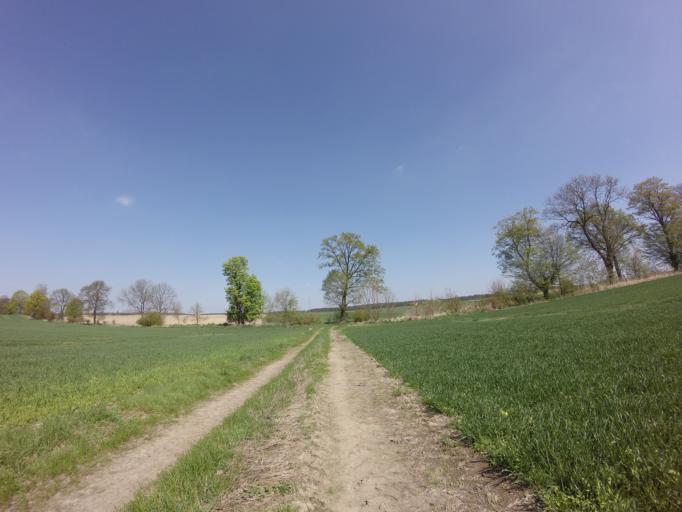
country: PL
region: West Pomeranian Voivodeship
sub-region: Powiat choszczenski
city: Choszczno
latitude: 53.1993
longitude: 15.3706
